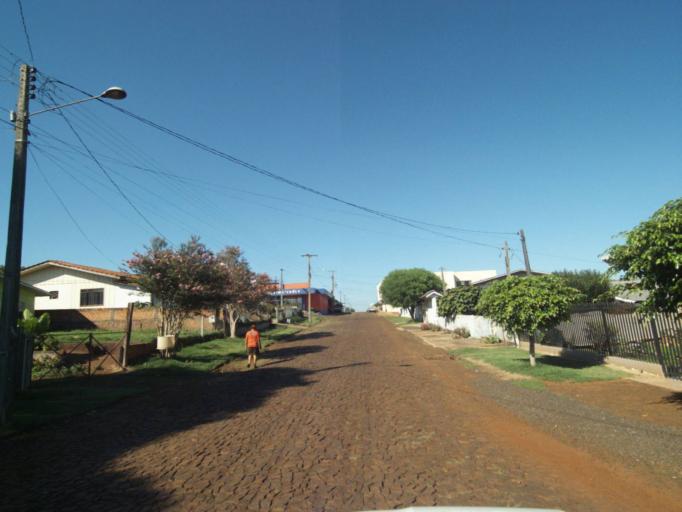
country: BR
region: Parana
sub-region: Laranjeiras Do Sul
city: Laranjeiras do Sul
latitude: -25.4918
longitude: -52.5318
